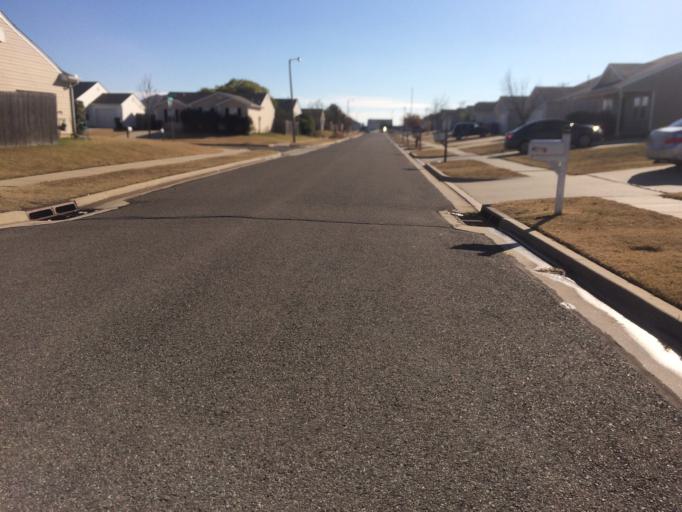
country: US
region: Oklahoma
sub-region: Cleveland County
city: Norman
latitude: 35.2504
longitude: -97.4496
